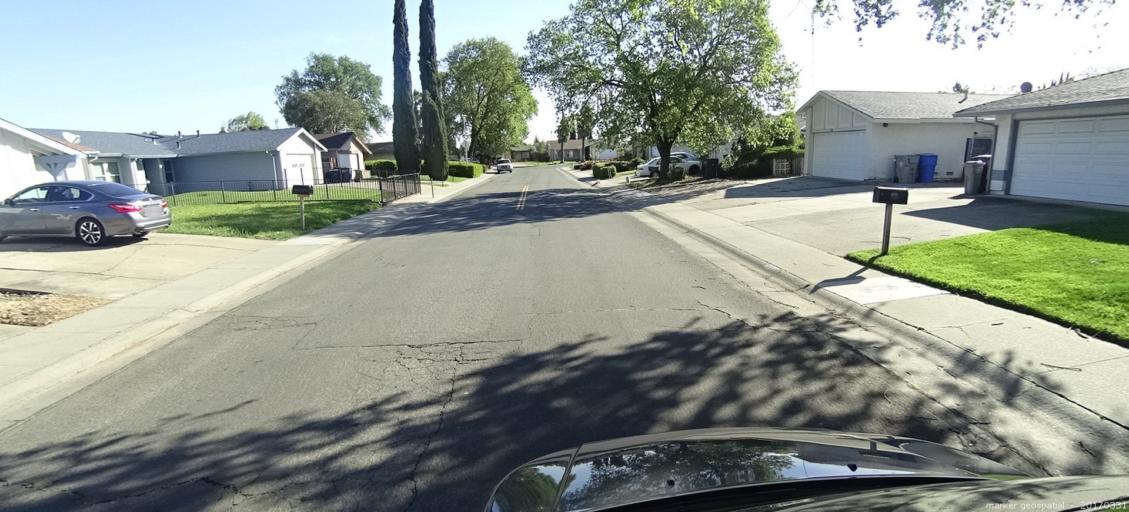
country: US
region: California
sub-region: Sacramento County
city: Parkway
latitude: 38.4719
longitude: -121.4532
